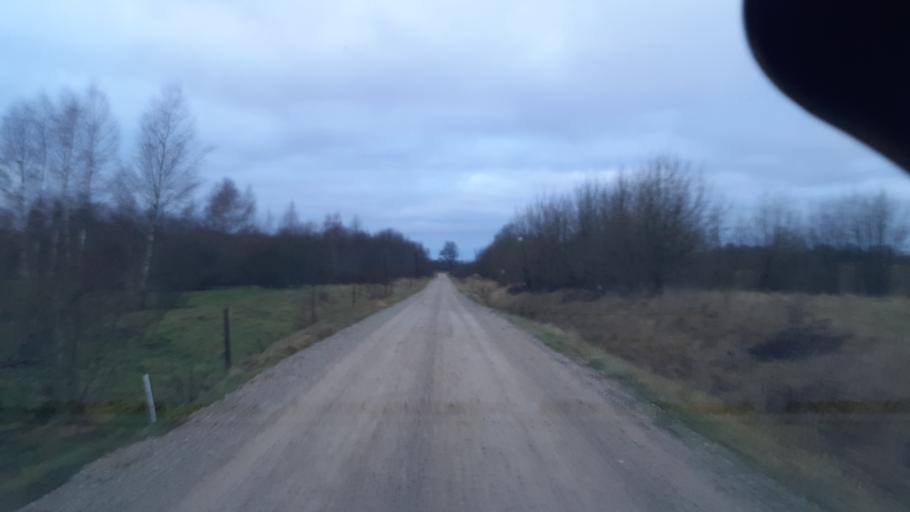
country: LV
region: Alsunga
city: Alsunga
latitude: 56.9044
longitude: 21.6892
